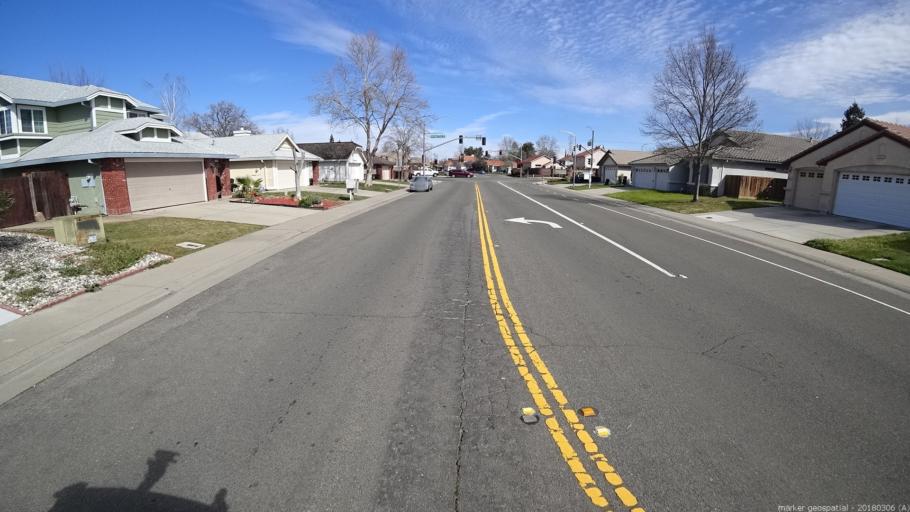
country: US
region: California
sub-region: Sacramento County
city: Vineyard
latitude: 38.4626
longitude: -121.3480
